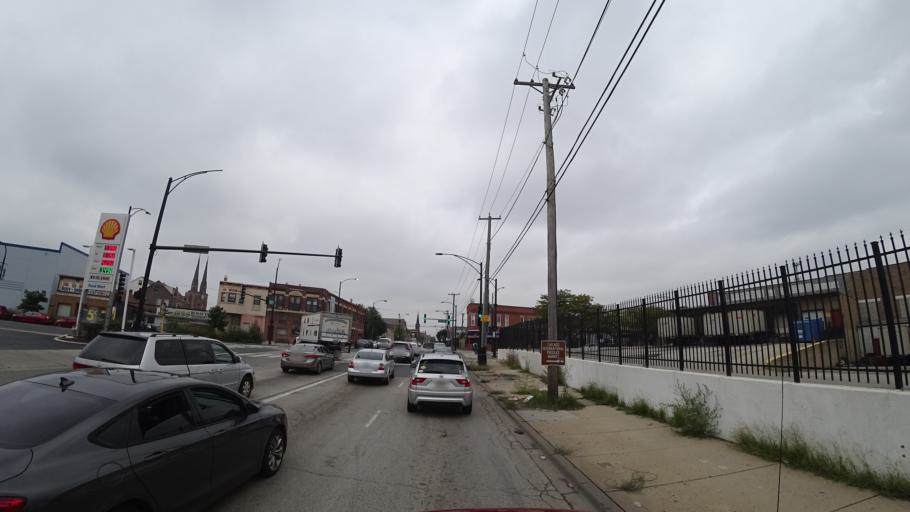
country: US
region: Illinois
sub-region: Cook County
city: Chicago
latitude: 41.8481
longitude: -87.6757
